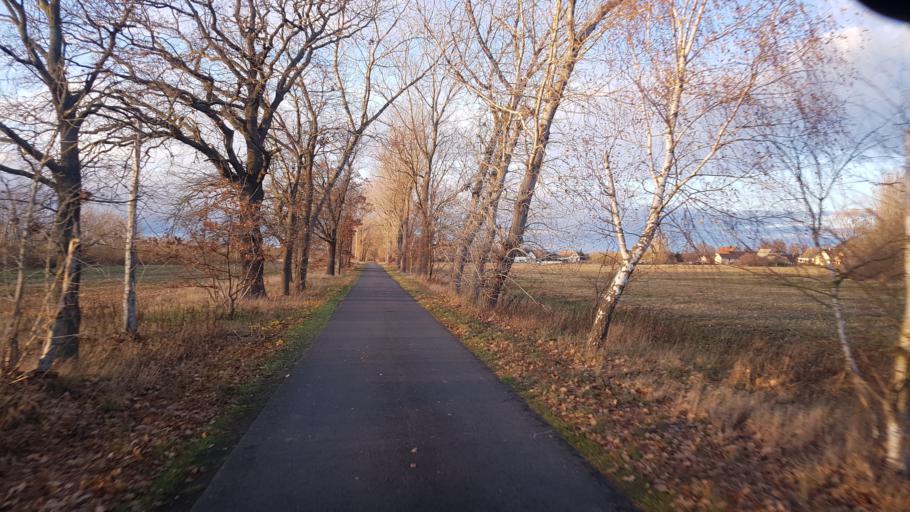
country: DE
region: Brandenburg
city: Falkenberg
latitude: 51.6373
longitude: 13.2648
